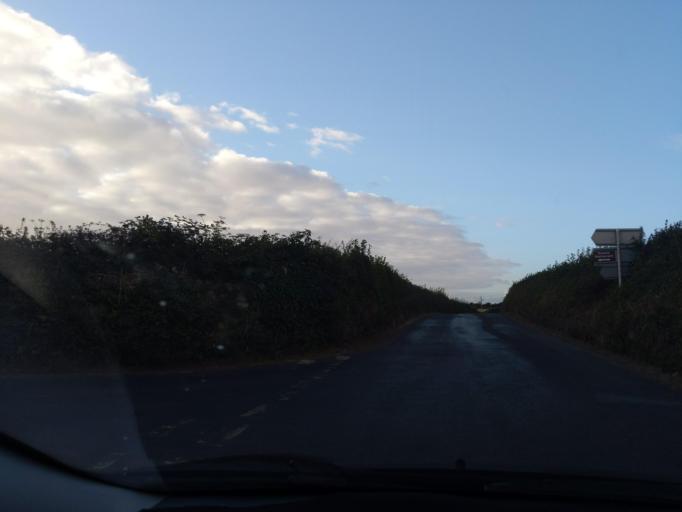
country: GB
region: England
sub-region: Devon
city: Salcombe
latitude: 50.2386
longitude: -3.8212
